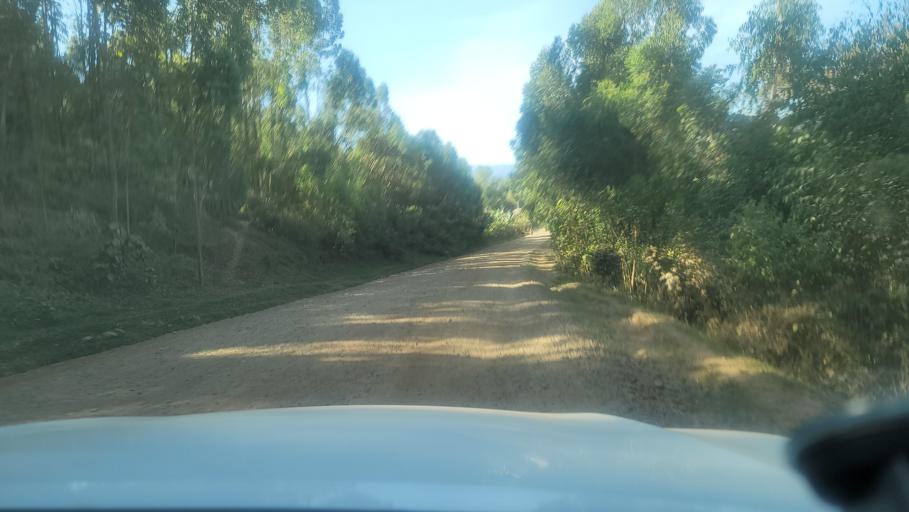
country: ET
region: Oromiya
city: Agaro
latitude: 7.8022
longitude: 36.4999
